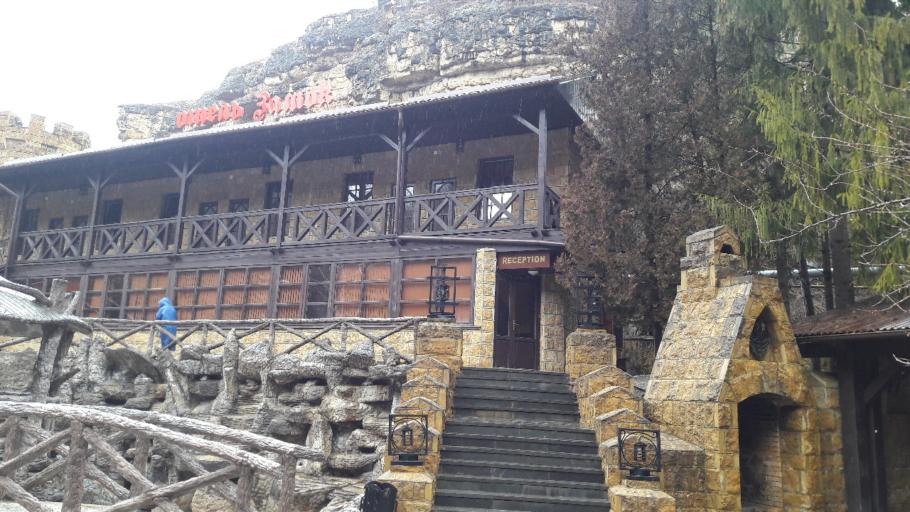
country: RU
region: Stavropol'skiy
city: Nezhinskiy
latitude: 43.8965
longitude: 42.6654
